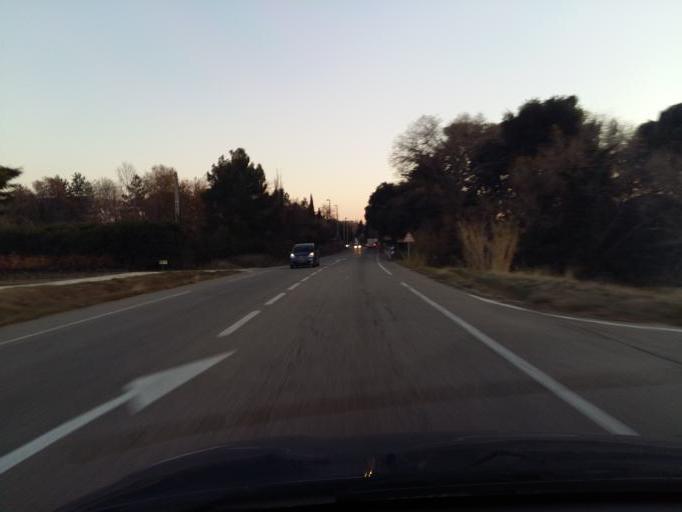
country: FR
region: Provence-Alpes-Cote d'Azur
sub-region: Departement du Vaucluse
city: Visan
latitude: 44.3205
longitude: 4.9479
